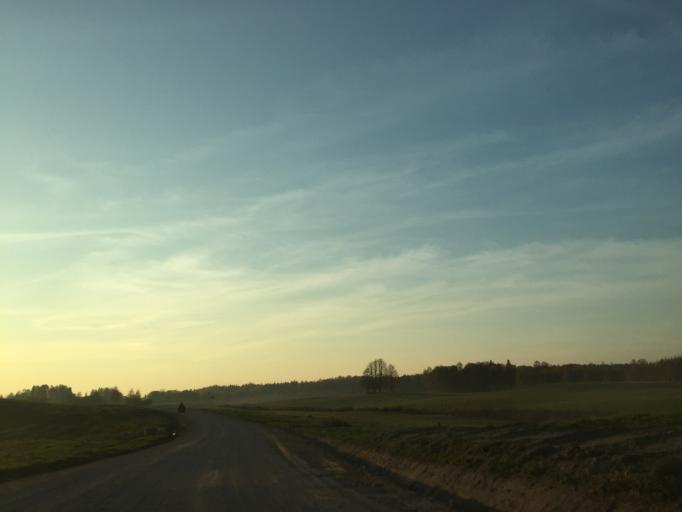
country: LV
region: Vainode
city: Vainode
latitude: 56.4817
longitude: 21.7466
